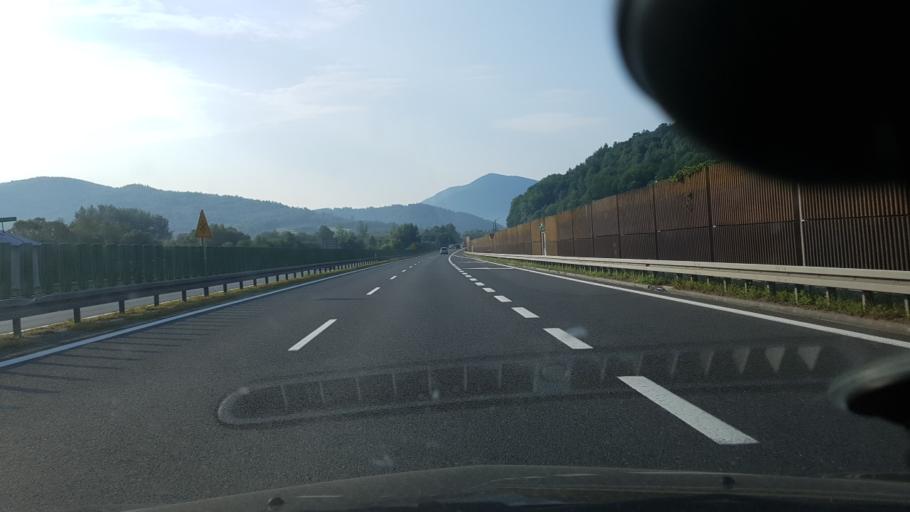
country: PL
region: Lesser Poland Voivodeship
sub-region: Powiat myslenicki
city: Pcim
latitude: 49.7475
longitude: 19.9738
